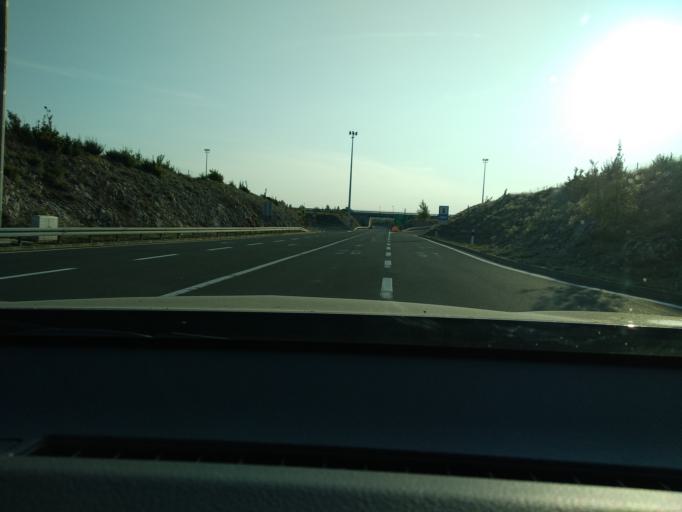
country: HR
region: Sibensko-Kniniska
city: Zaton
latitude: 43.8875
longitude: 15.7872
